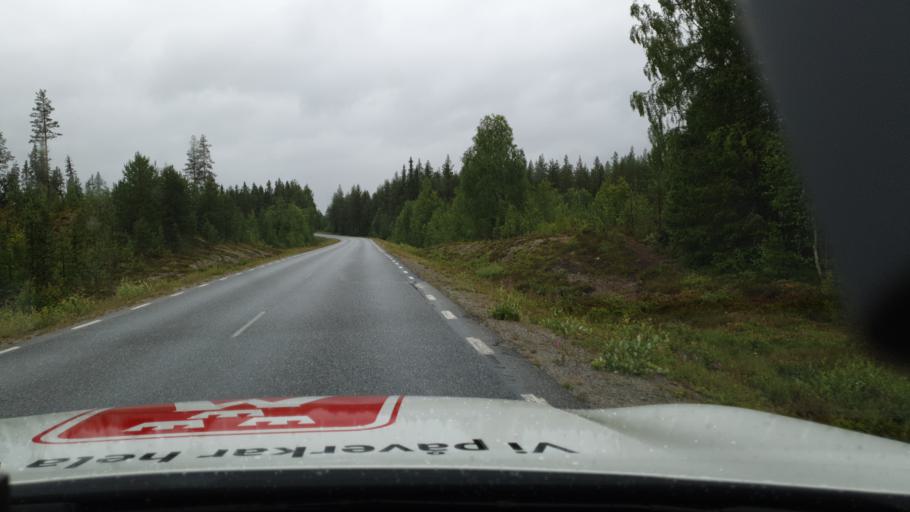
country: SE
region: Vaesterbotten
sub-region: Asele Kommun
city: Asele
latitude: 64.2875
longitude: 17.2605
